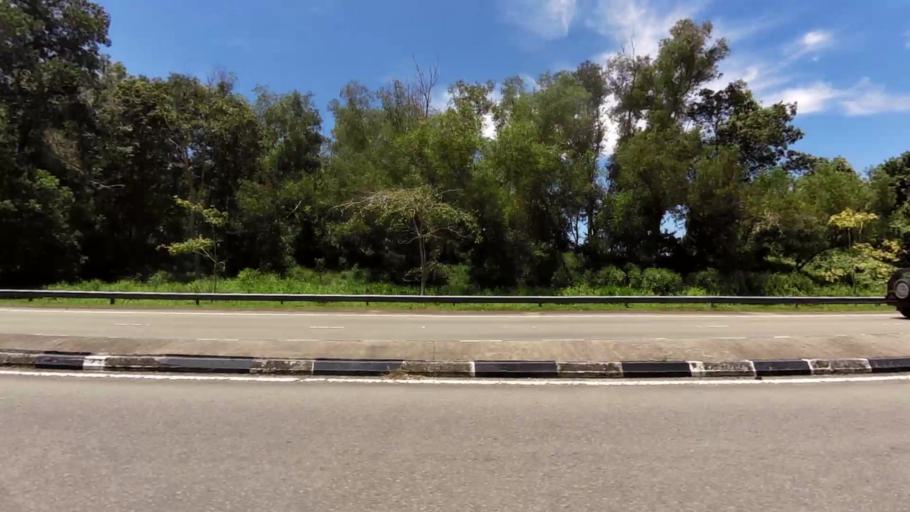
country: BN
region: Brunei and Muara
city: Bandar Seri Begawan
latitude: 4.9208
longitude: 114.9538
